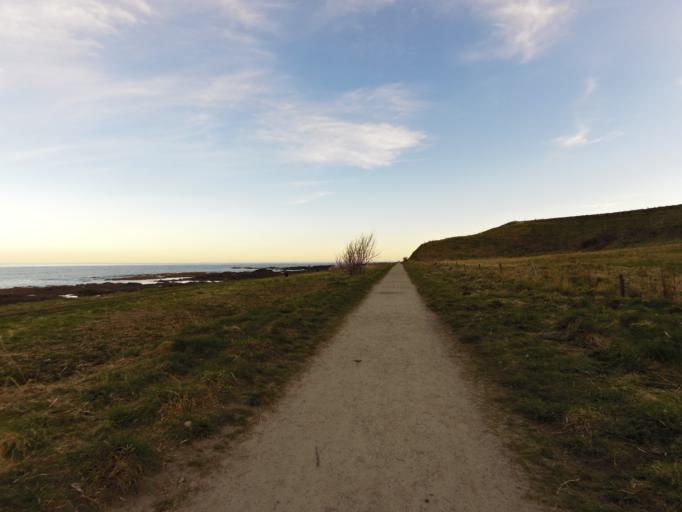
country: GB
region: Scotland
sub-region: Aberdeenshire
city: Inverbervie
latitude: 56.8382
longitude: -2.2758
